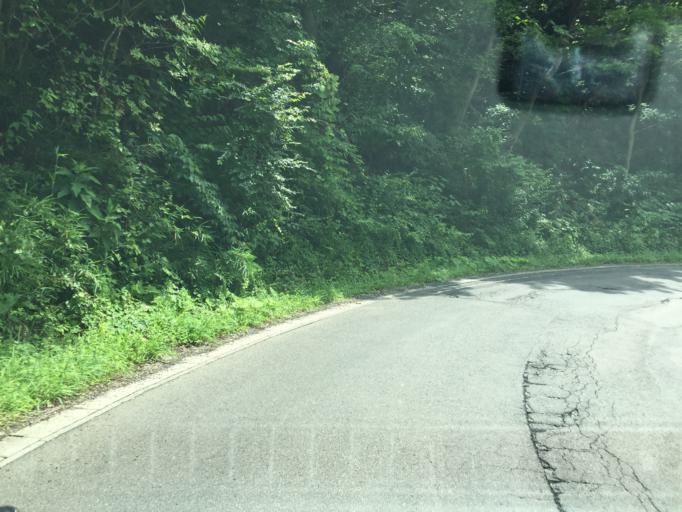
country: JP
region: Fukushima
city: Fukushima-shi
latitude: 37.7479
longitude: 140.5100
